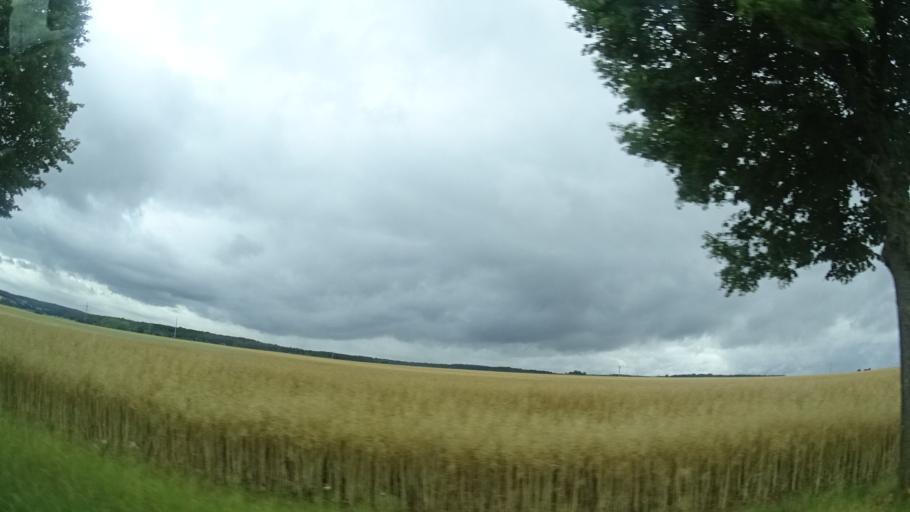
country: LU
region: Luxembourg
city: Aspelt
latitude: 49.5279
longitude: 6.2370
